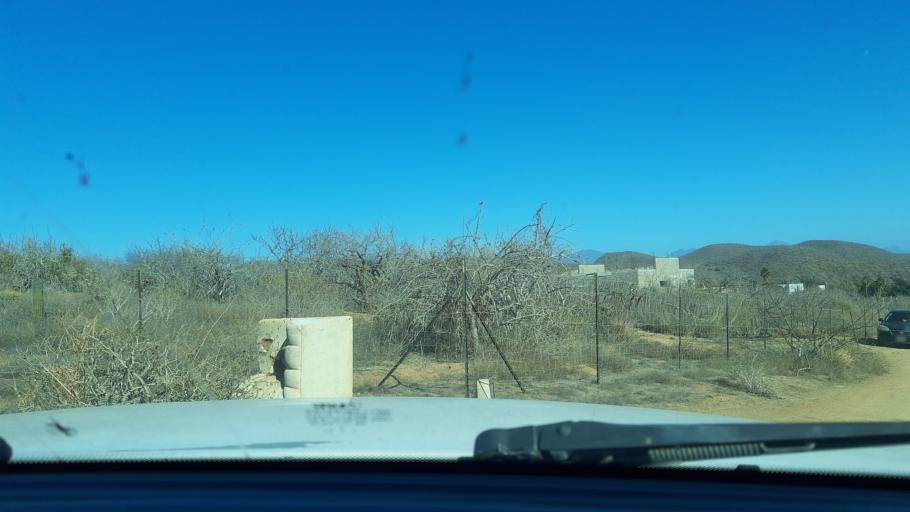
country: MX
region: Baja California Sur
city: Todos Santos
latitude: 23.4734
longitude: -110.2209
